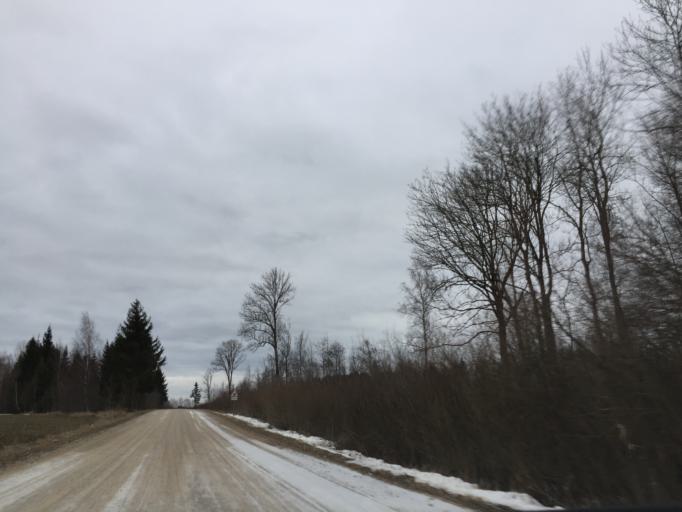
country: LT
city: Zagare
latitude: 56.3029
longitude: 23.2597
